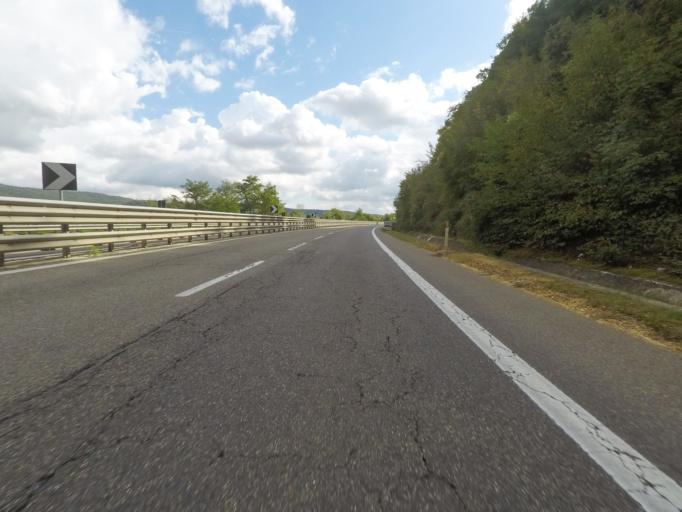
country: IT
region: Tuscany
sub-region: Provincia di Siena
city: Rapolano Terme
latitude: 43.2892
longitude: 11.6194
